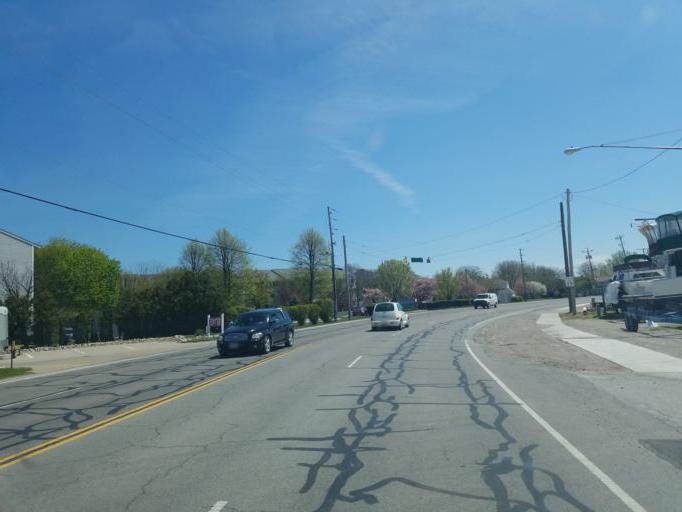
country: US
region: Ohio
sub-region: Ottawa County
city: Port Clinton
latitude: 41.5173
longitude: -82.9443
